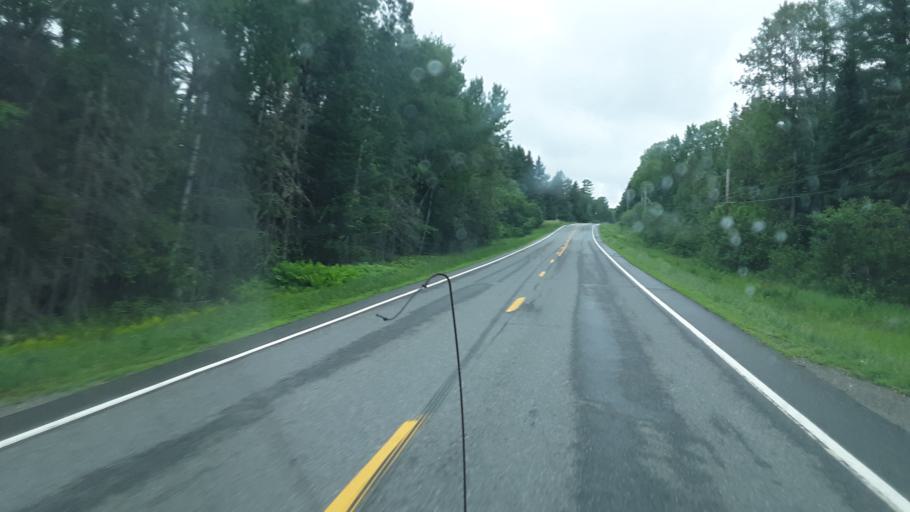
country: US
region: Maine
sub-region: Aroostook County
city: Presque Isle
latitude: 46.4731
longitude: -68.3885
